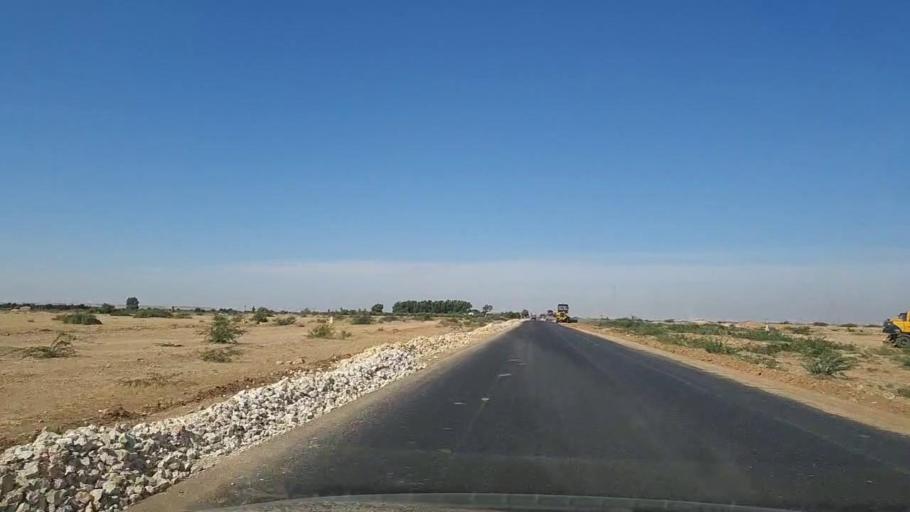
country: PK
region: Sindh
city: Kotri
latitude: 25.2587
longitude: 68.2235
